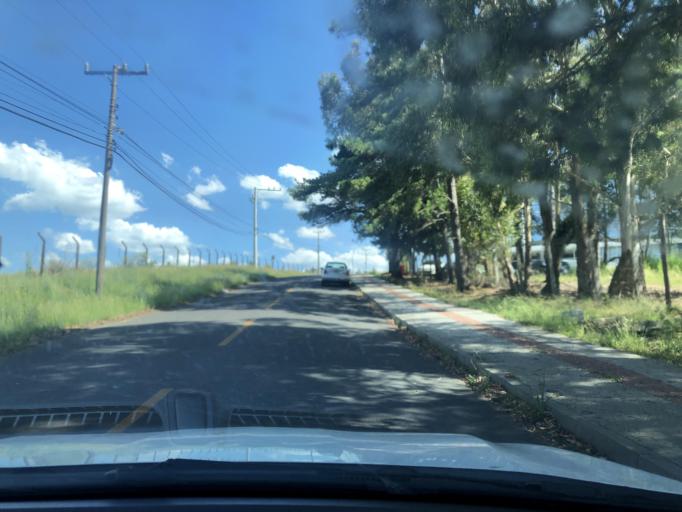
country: BR
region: Santa Catarina
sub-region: Lages
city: Lages
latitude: -27.8009
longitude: -50.3369
